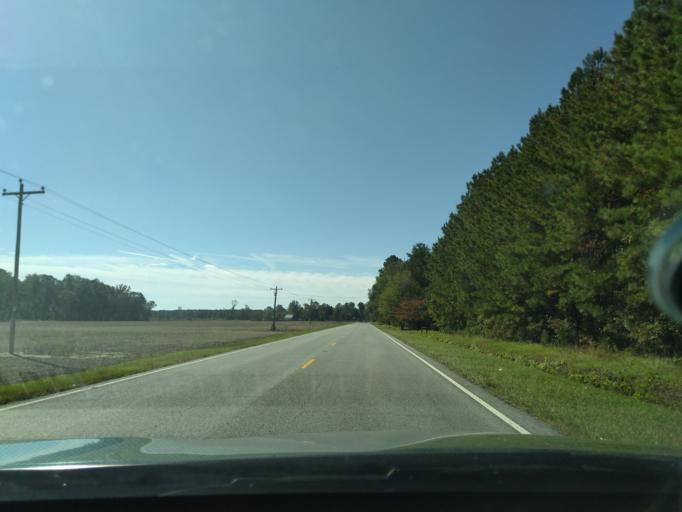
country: US
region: North Carolina
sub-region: Washington County
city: Plymouth
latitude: 35.6650
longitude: -76.7904
